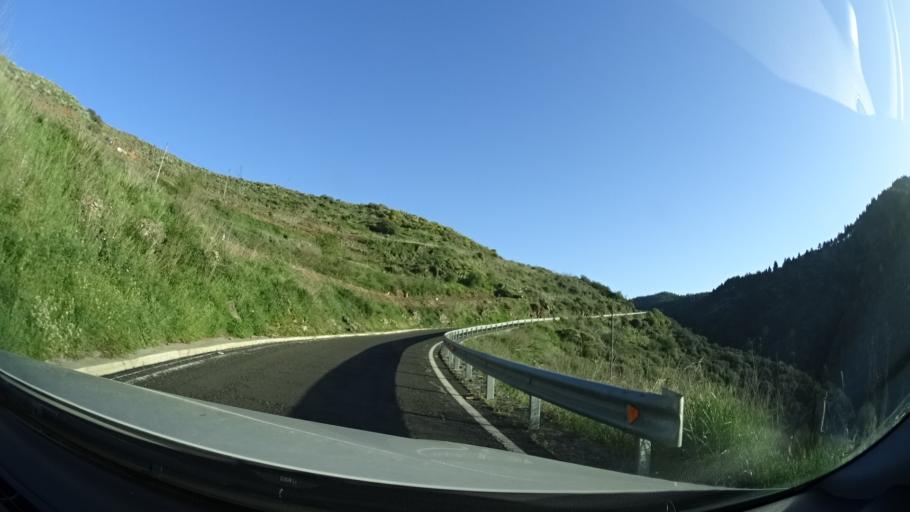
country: ES
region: Canary Islands
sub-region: Provincia de Las Palmas
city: Artenara
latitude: 28.0370
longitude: -15.6719
